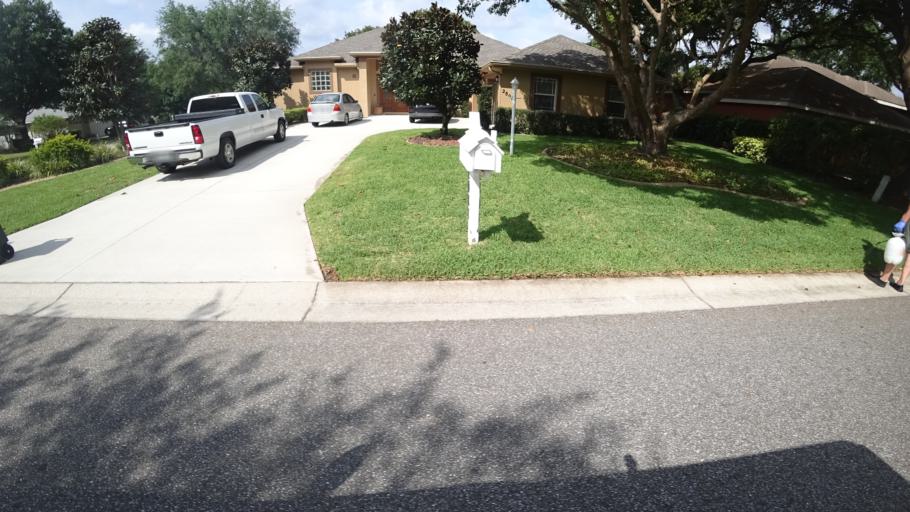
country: US
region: Florida
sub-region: Manatee County
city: Ellenton
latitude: 27.5382
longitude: -82.4484
